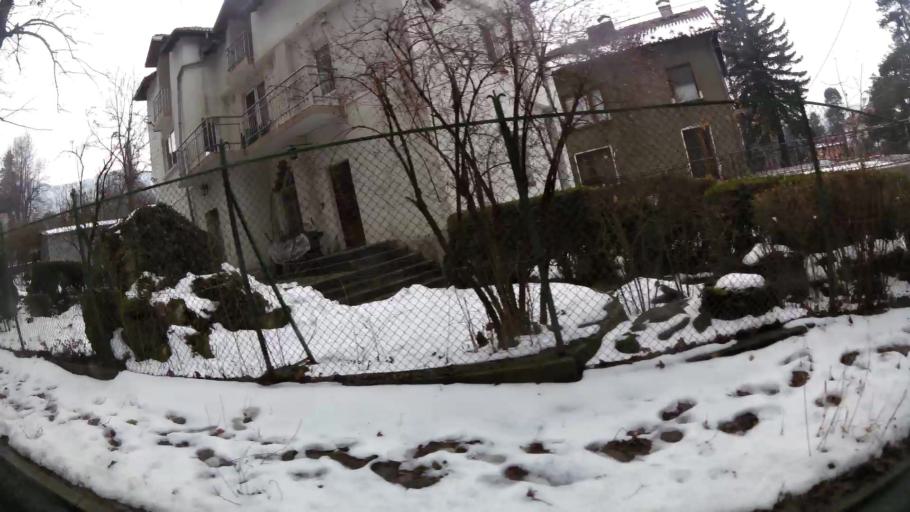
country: BG
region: Sofia-Capital
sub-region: Stolichna Obshtina
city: Sofia
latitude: 42.6552
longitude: 23.2384
